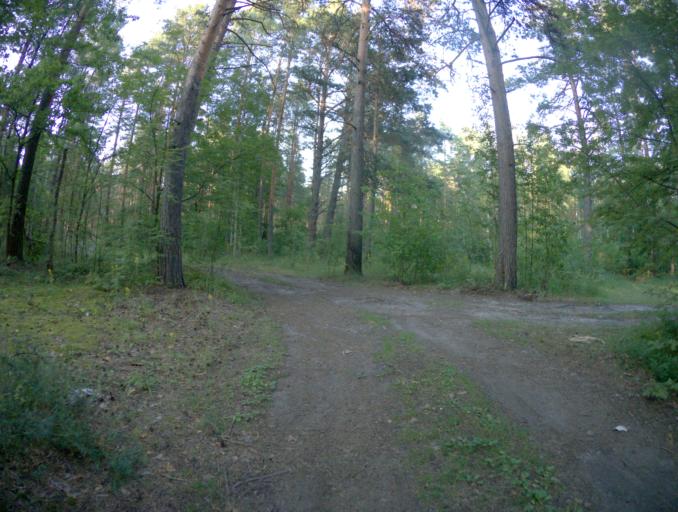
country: RU
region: Vladimir
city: Kommunar
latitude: 56.0954
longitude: 40.4510
